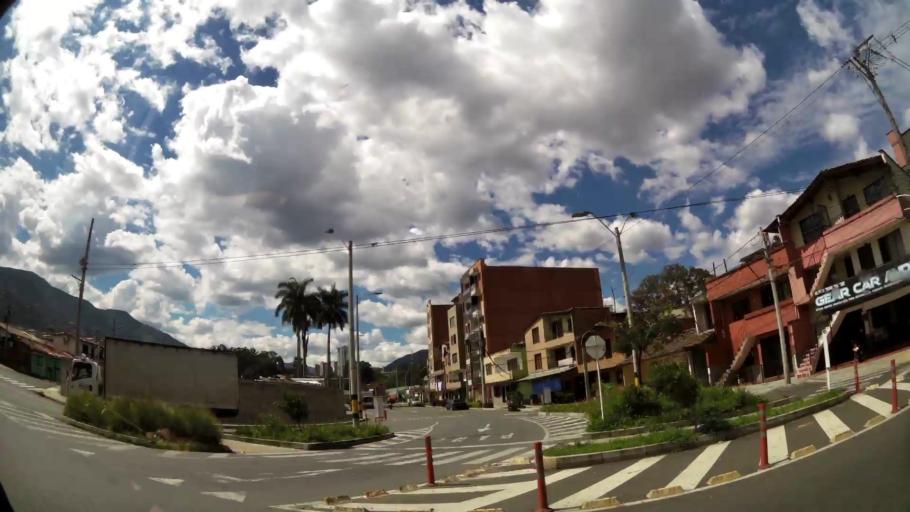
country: CO
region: Antioquia
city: Sabaneta
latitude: 6.1524
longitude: -75.6234
